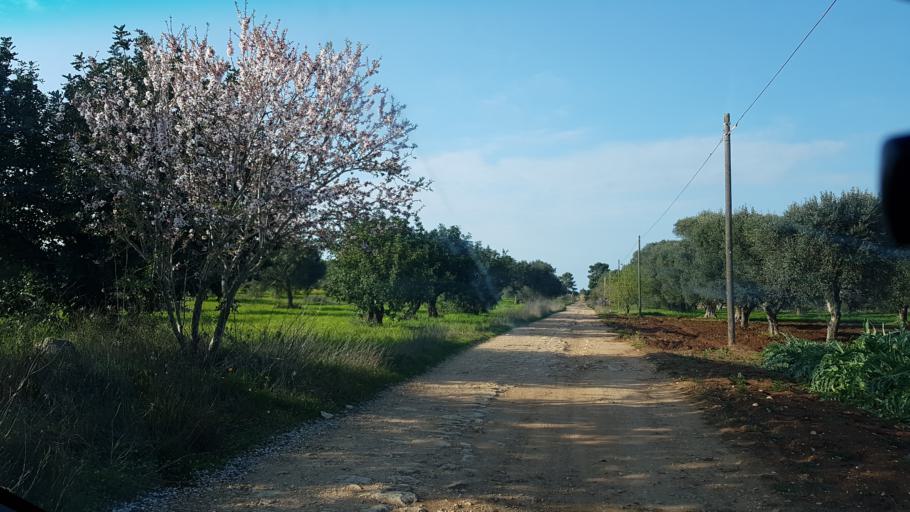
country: IT
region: Apulia
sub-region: Provincia di Brindisi
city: San Vito dei Normanni
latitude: 40.6771
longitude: 17.7897
